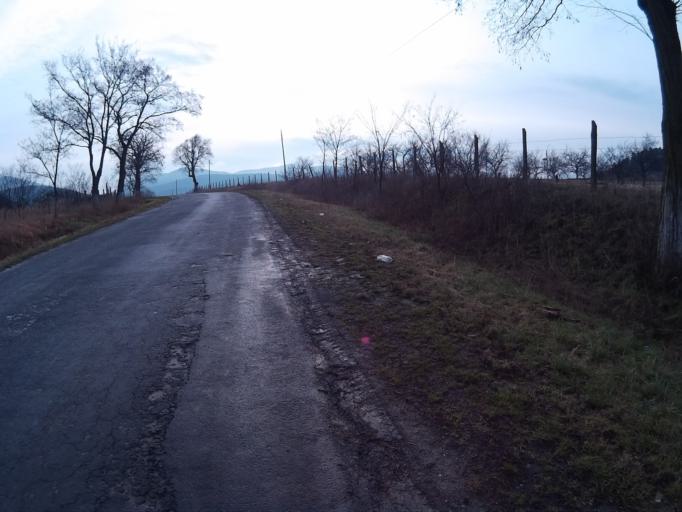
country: HU
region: Borsod-Abauj-Zemplen
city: Abaujszanto
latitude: 48.3418
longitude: 21.2186
